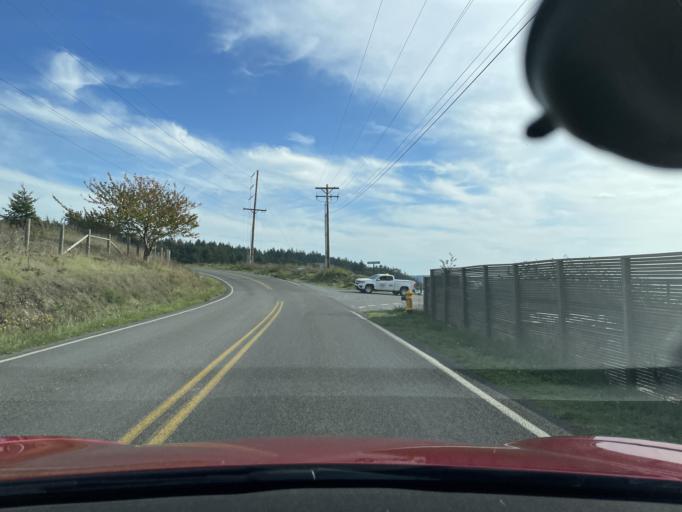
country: US
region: Washington
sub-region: San Juan County
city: Friday Harbor
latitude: 48.5216
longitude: -123.0088
